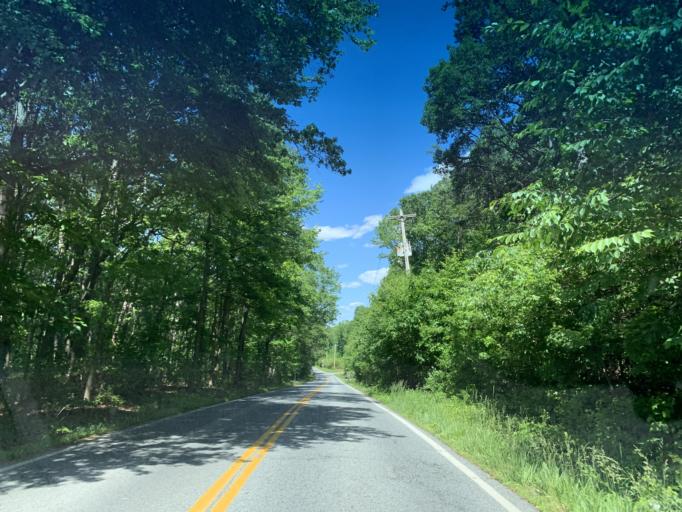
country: US
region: Maryland
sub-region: Cecil County
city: North East
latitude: 39.5615
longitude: -75.8909
